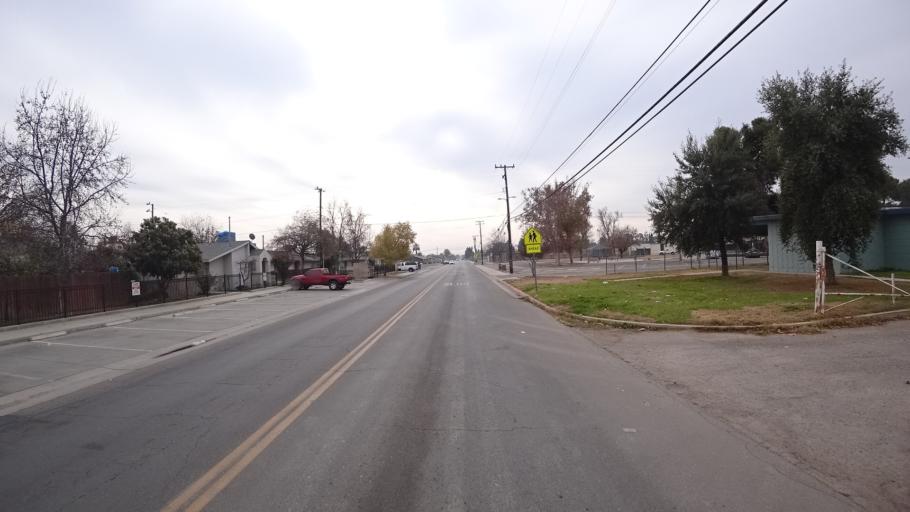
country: US
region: California
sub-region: Kern County
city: Bakersfield
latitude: 35.3676
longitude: -118.9909
